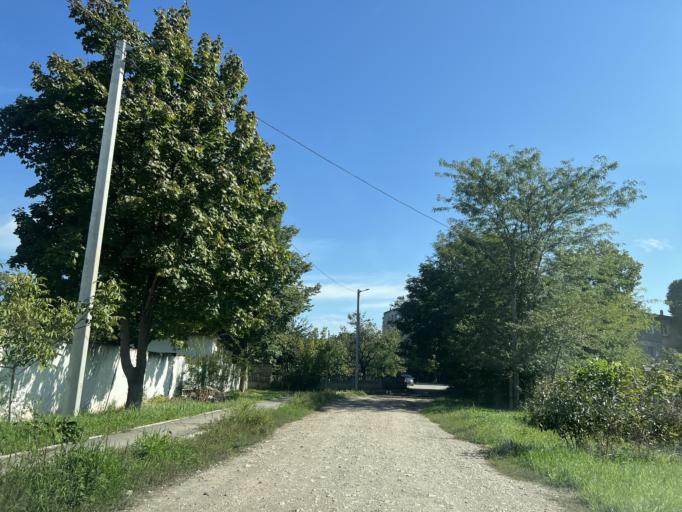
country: RO
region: Iasi
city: Ungheni-Prut
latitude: 47.1962
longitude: 27.7921
